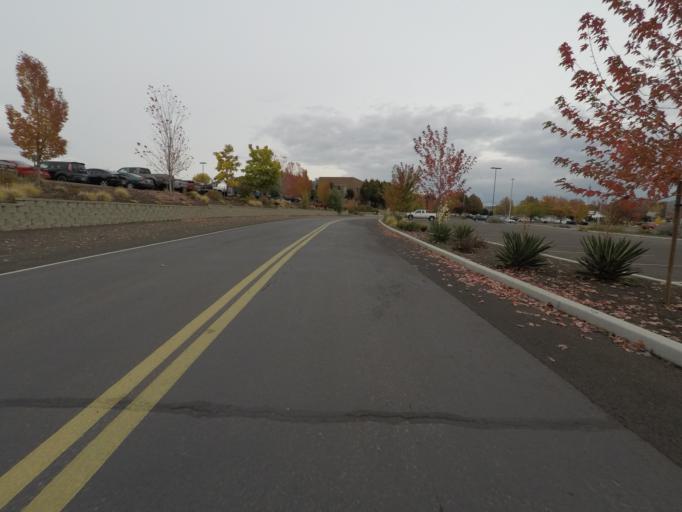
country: US
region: Washington
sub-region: Walla Walla County
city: Walla Walla East
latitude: 46.0800
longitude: -118.2791
